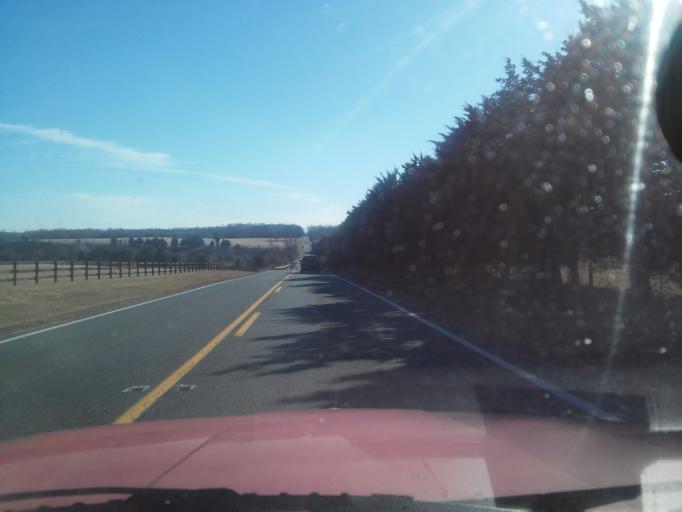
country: US
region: Virginia
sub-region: Orange County
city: Gordonsville
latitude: 38.0232
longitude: -78.1907
